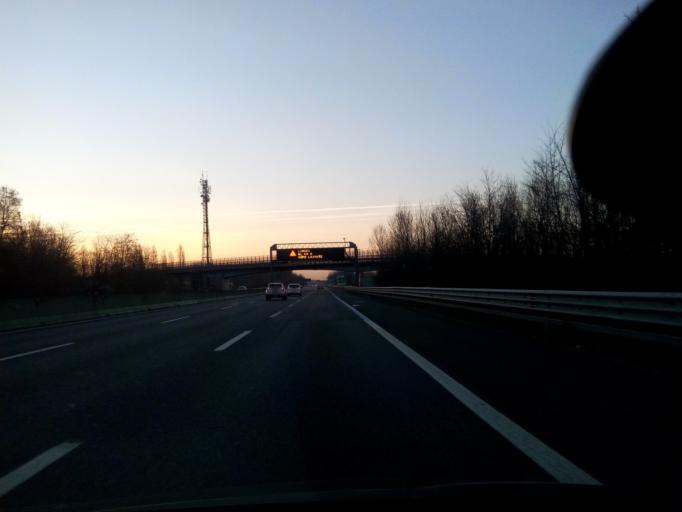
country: IT
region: Lombardy
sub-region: Citta metropolitana di Milano
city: Cantalupo
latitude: 45.5841
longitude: 8.9901
